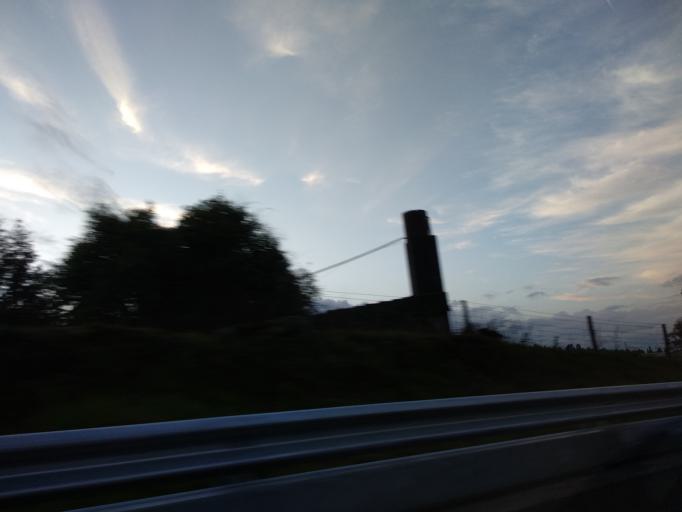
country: PT
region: Braga
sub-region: Braga
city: Oliveira
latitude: 41.4876
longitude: -8.4666
